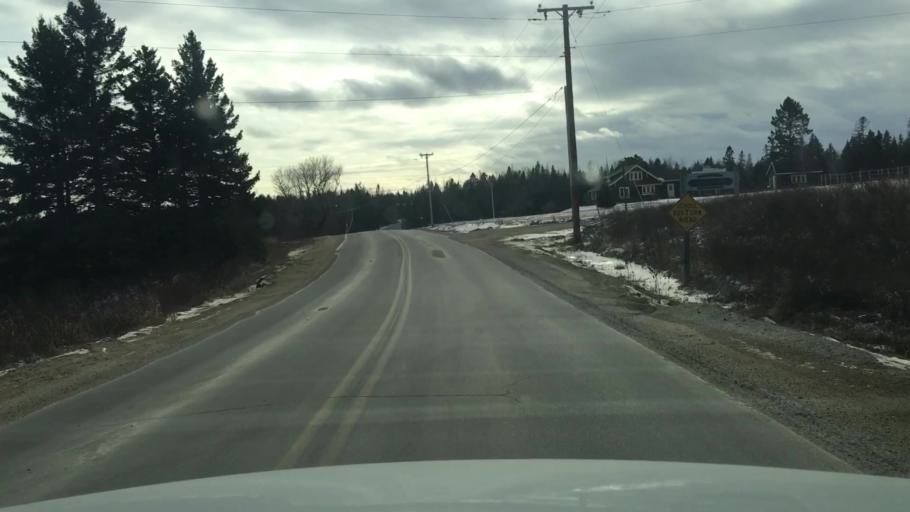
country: US
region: Maine
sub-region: Washington County
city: Jonesport
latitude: 44.6309
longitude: -67.5959
